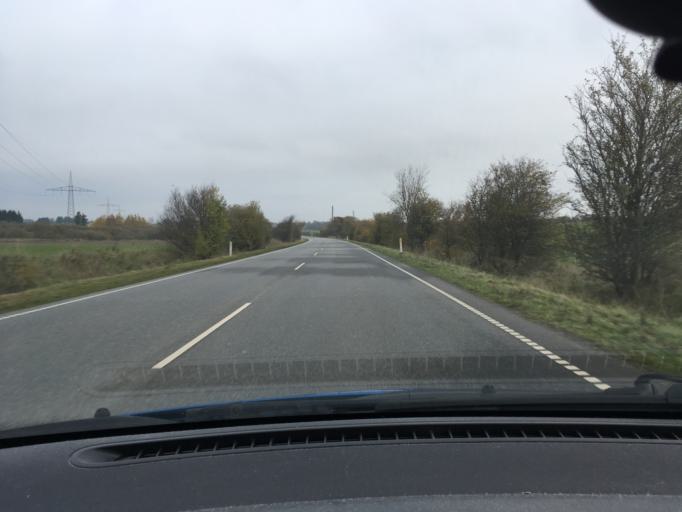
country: DK
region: South Denmark
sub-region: Aabenraa Kommune
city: Aabenraa
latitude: 54.9943
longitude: 9.4120
